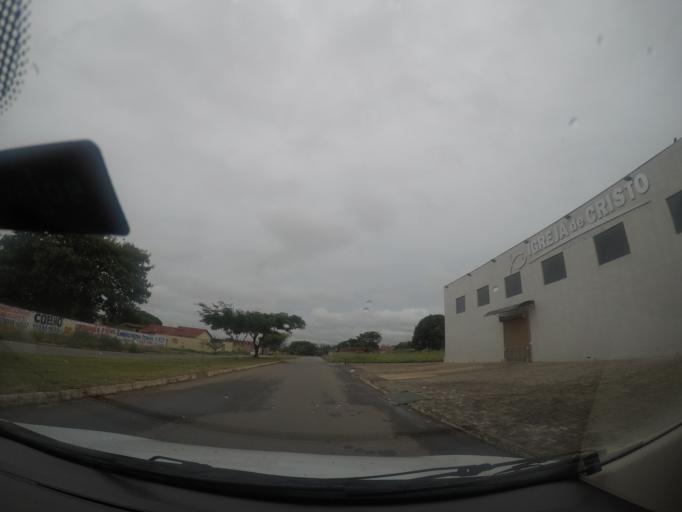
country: BR
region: Goias
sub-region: Goiania
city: Goiania
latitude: -16.7439
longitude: -49.3289
